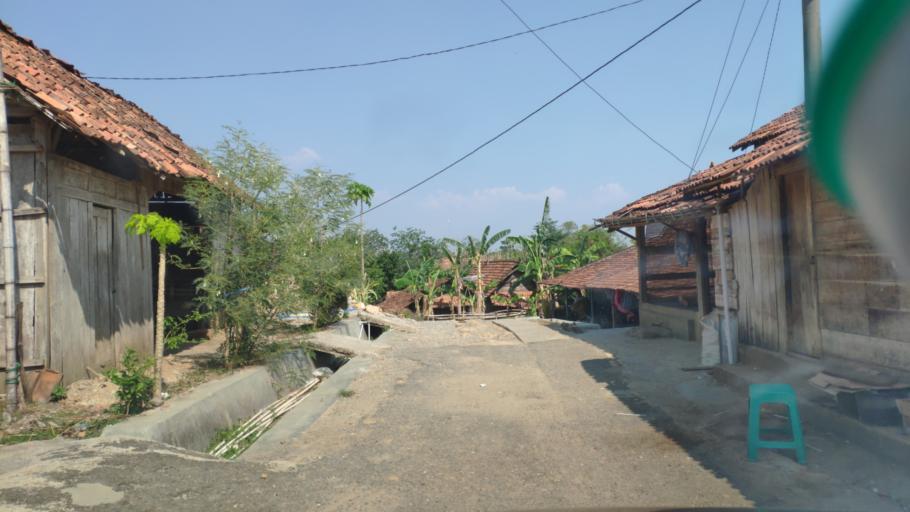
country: ID
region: Central Java
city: Ngapus
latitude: -6.9297
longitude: 111.2065
